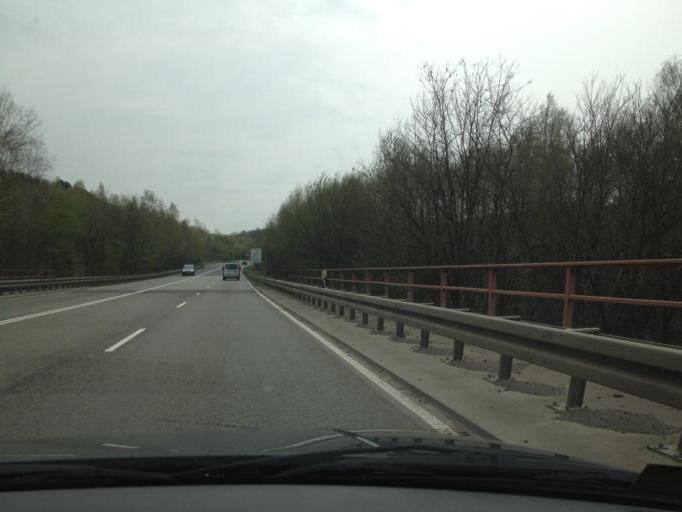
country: DE
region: Saarland
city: Neunkirchen
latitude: 49.3379
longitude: 7.1532
